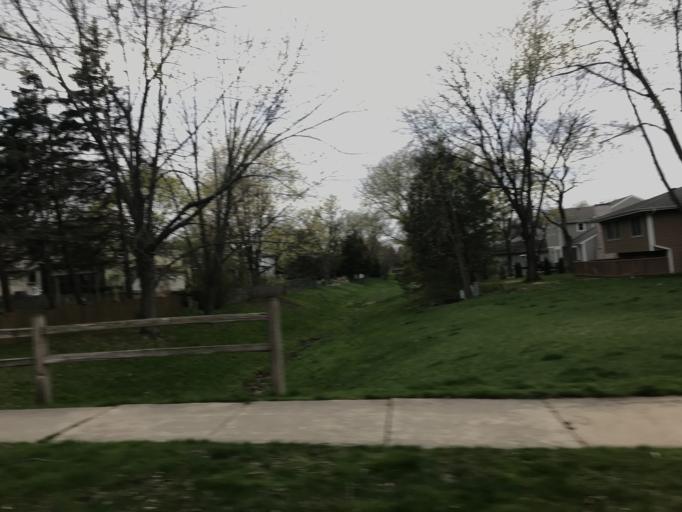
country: US
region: Illinois
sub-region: Will County
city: Bolingbrook
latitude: 41.7375
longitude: -88.1086
